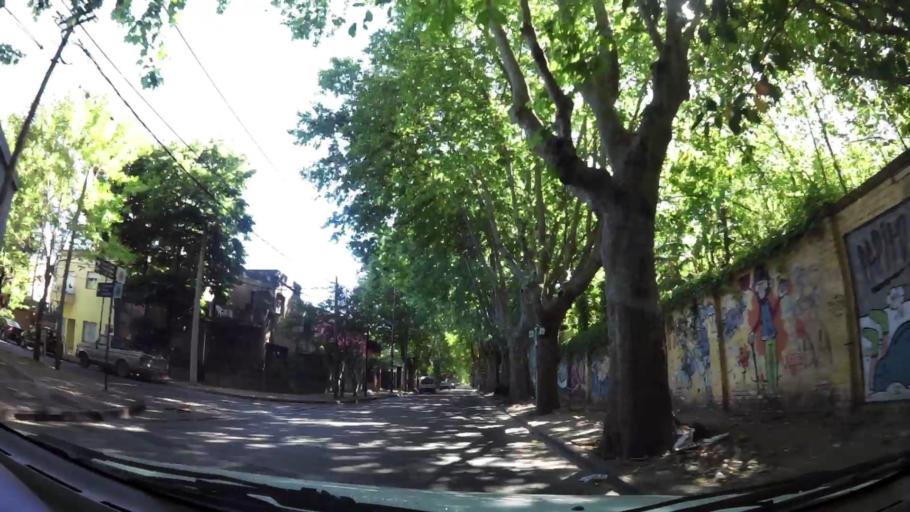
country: AR
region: Buenos Aires
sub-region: Partido de San Isidro
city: San Isidro
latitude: -34.4662
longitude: -58.5244
